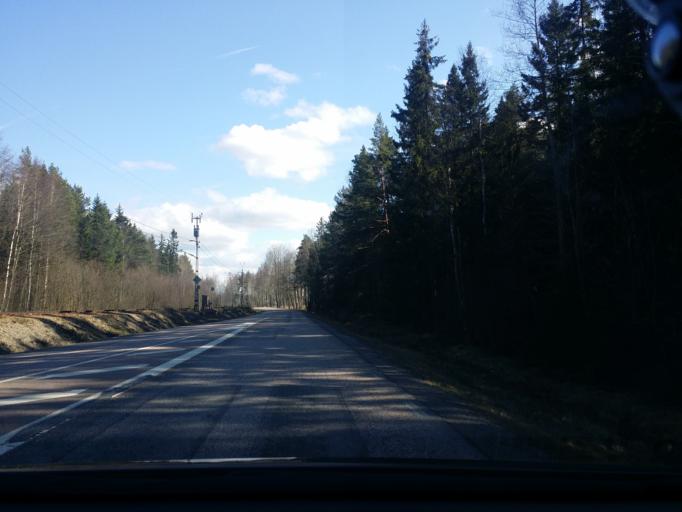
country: SE
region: Vaestmanland
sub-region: Sala Kommun
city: Sala
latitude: 59.9667
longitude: 16.5062
